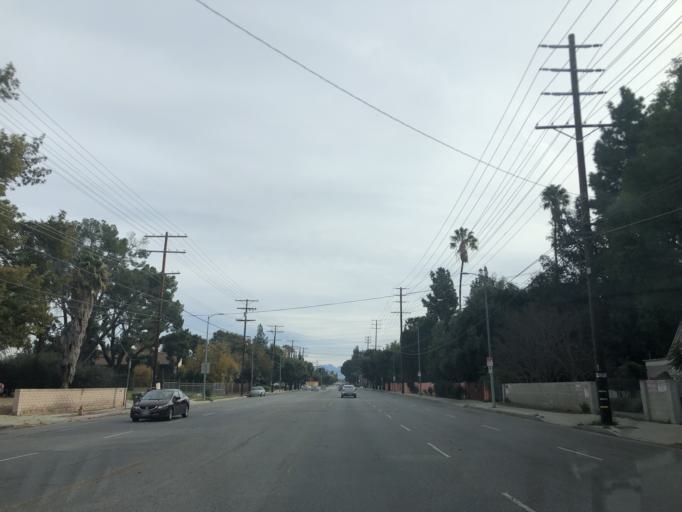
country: US
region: California
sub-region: Los Angeles County
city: Northridge
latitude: 34.2355
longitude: -118.5475
